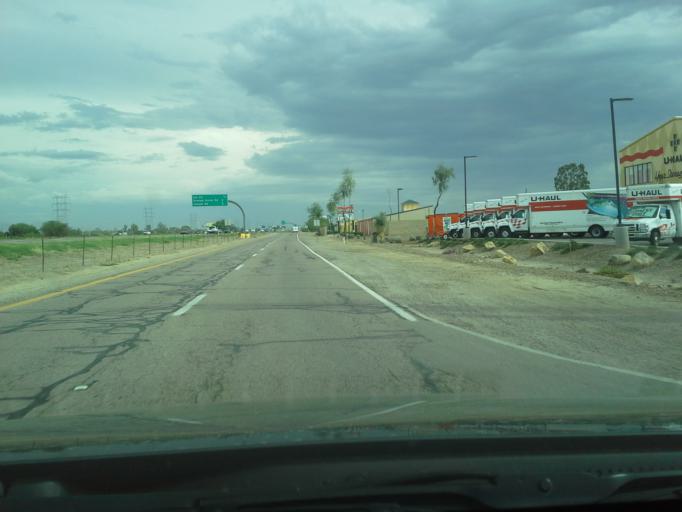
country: US
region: Arizona
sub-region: Pima County
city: Casas Adobes
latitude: 32.3468
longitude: -111.0771
